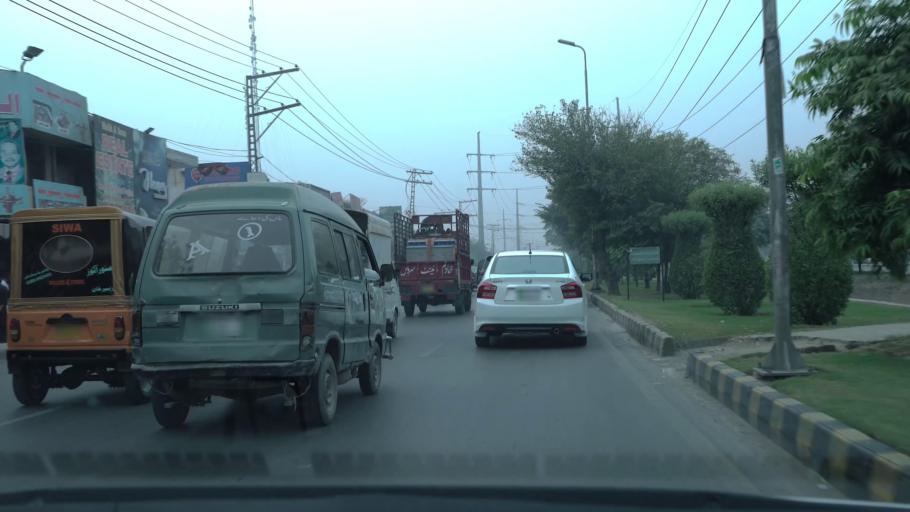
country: PK
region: Punjab
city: Lahore
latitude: 31.4786
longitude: 74.3006
